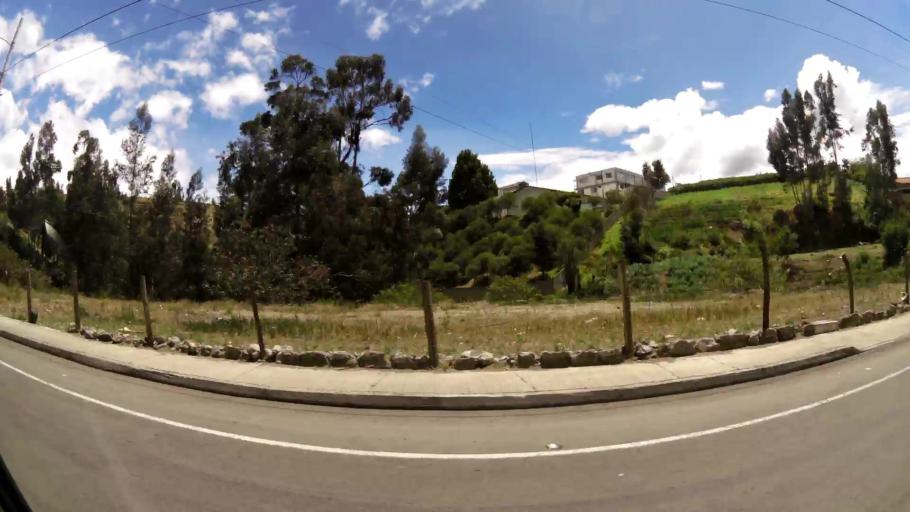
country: EC
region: Tungurahua
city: Pelileo
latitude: -1.3209
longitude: -78.5951
